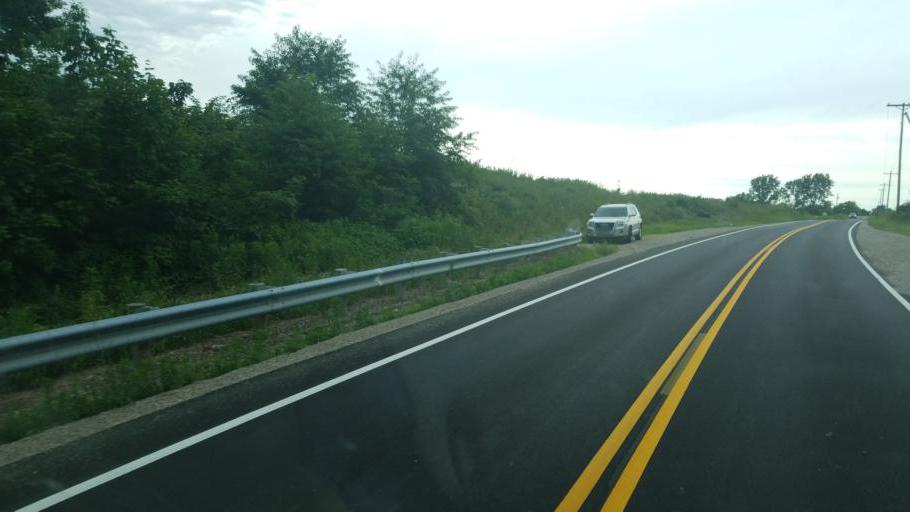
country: US
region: Ohio
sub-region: Delaware County
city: Ashley
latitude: 40.3568
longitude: -82.9221
